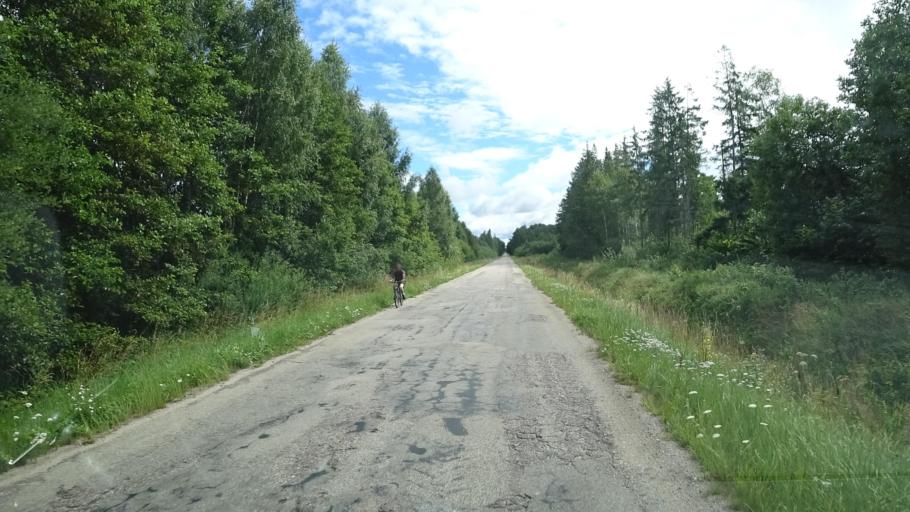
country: LV
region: Grobina
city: Grobina
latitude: 56.6566
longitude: 21.0979
